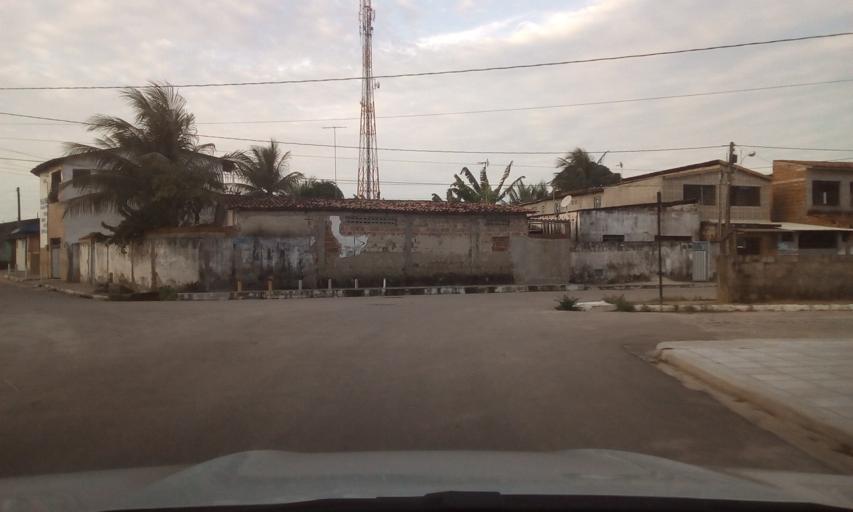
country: BR
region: Paraiba
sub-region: Conde
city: Conde
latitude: -7.2118
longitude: -34.8402
